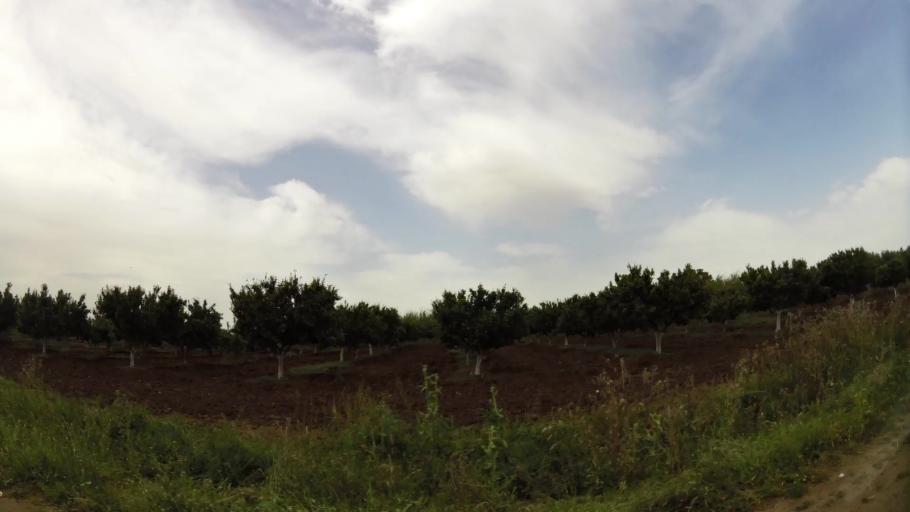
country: MA
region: Rabat-Sale-Zemmour-Zaer
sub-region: Khemisset
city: Khemisset
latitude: 33.7461
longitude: -6.2001
